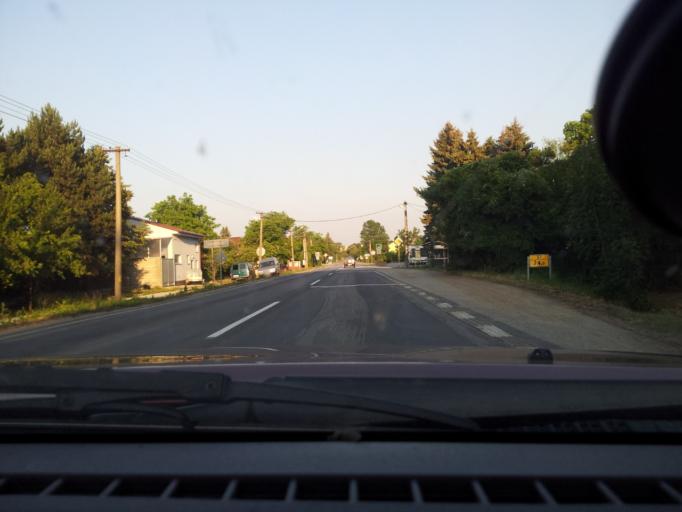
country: SK
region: Trnavsky
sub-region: Okres Skalica
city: Skalica
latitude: 48.7697
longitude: 17.2788
